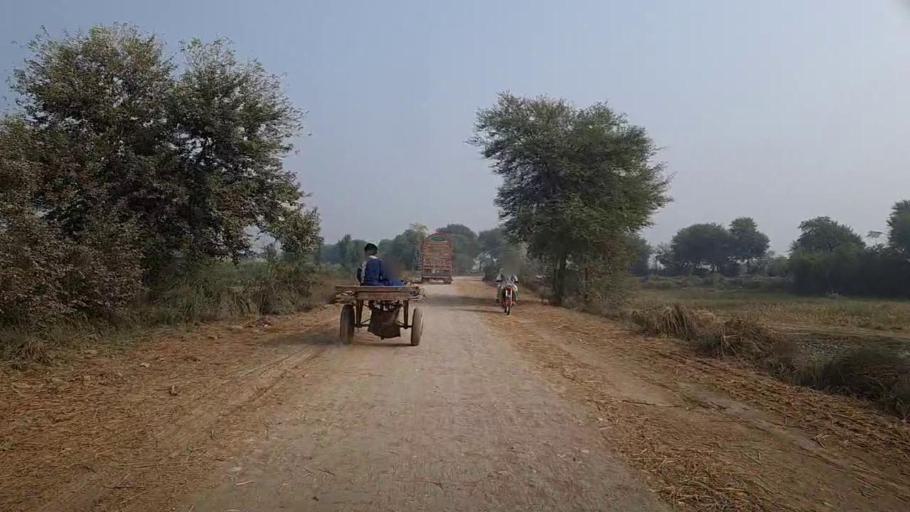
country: PK
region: Sindh
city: Dadu
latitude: 26.8391
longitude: 67.7782
